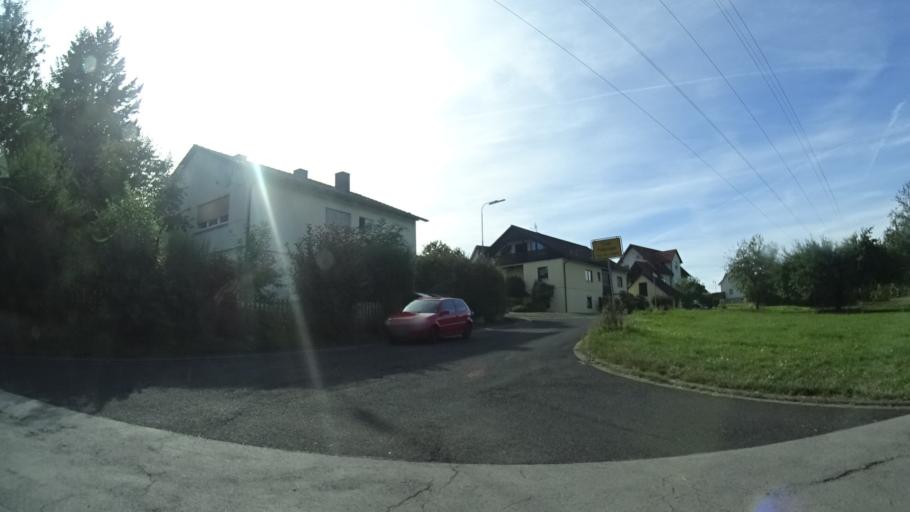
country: DE
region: Bavaria
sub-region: Regierungsbezirk Unterfranken
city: Fladungen
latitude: 50.5245
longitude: 10.1471
